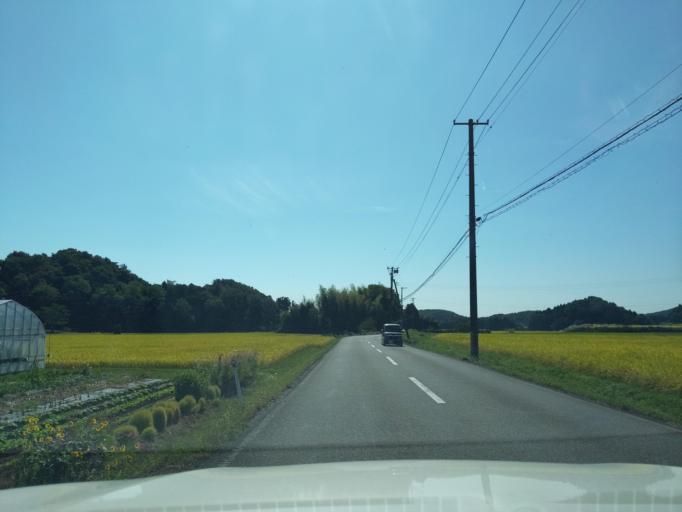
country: JP
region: Fukushima
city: Koriyama
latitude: 37.3844
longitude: 140.2607
